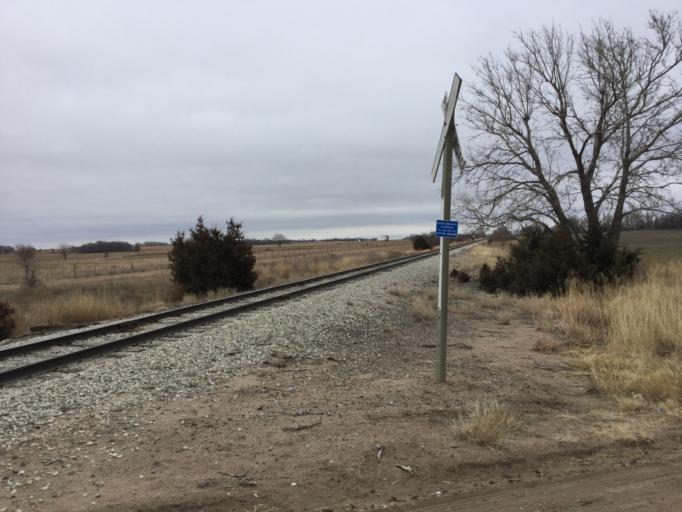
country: US
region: Kansas
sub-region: Barton County
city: Ellinwood
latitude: 38.3001
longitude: -98.4614
